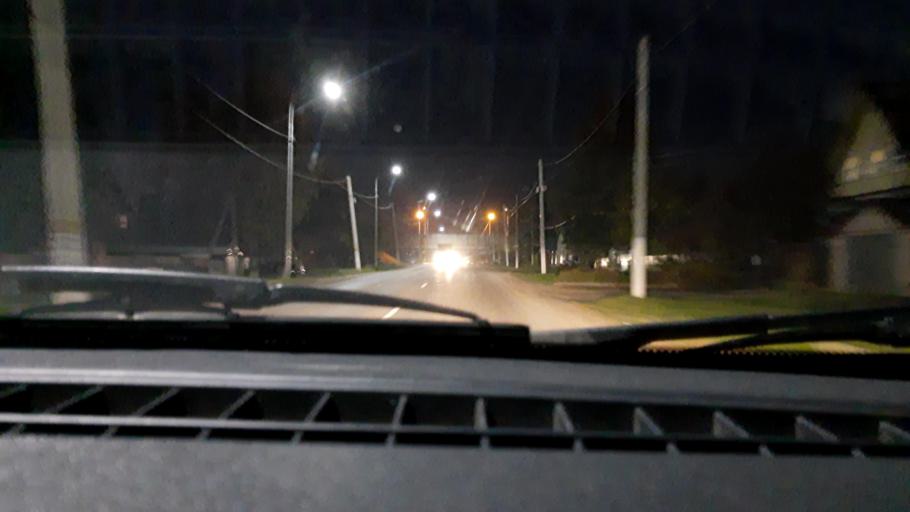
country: RU
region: Bashkortostan
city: Mikhaylovka
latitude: 54.7995
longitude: 55.8915
